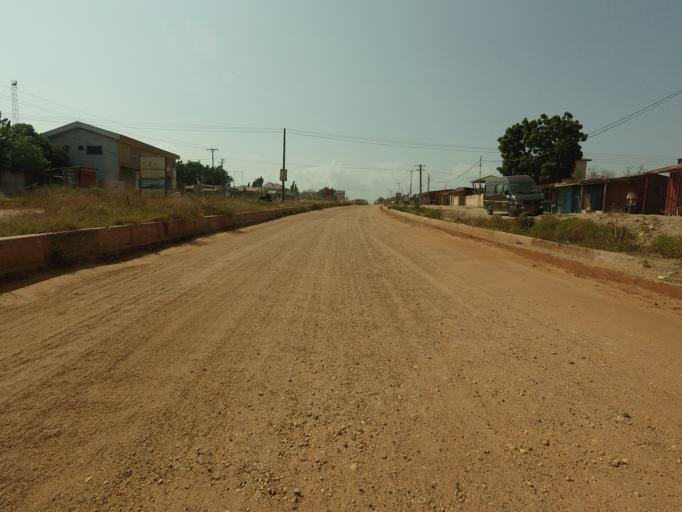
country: GH
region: Greater Accra
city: Teshi Old Town
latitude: 5.6059
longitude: -0.1222
